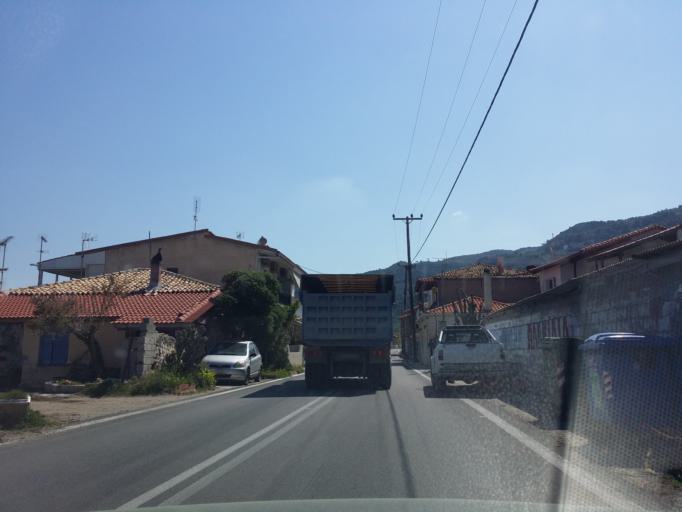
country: GR
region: West Greece
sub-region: Nomos Achaias
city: Aiyira
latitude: 38.1330
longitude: 22.4062
